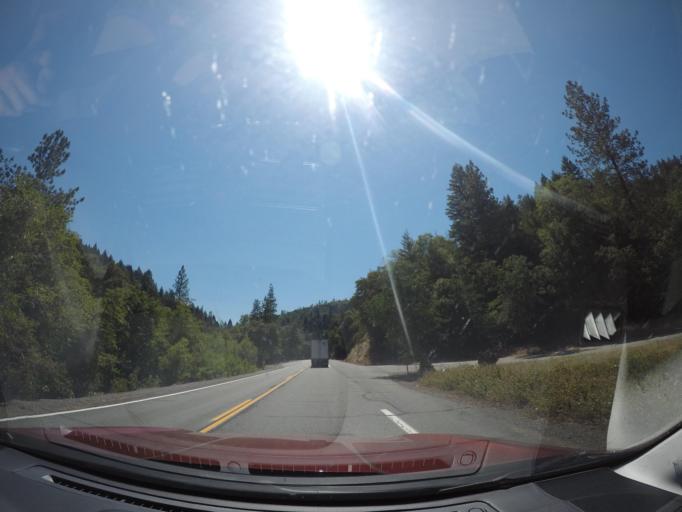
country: US
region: California
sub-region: Shasta County
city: Bella Vista
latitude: 40.7434
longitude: -122.0666
